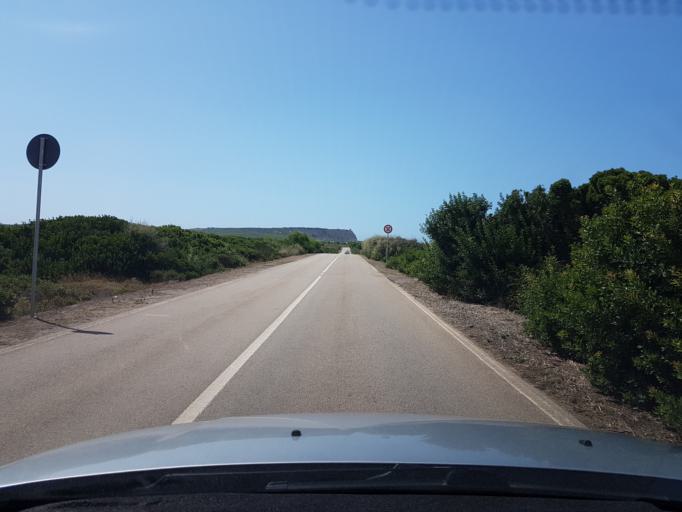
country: IT
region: Sardinia
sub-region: Provincia di Oristano
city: Riola Sardo
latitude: 40.0398
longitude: 8.4110
